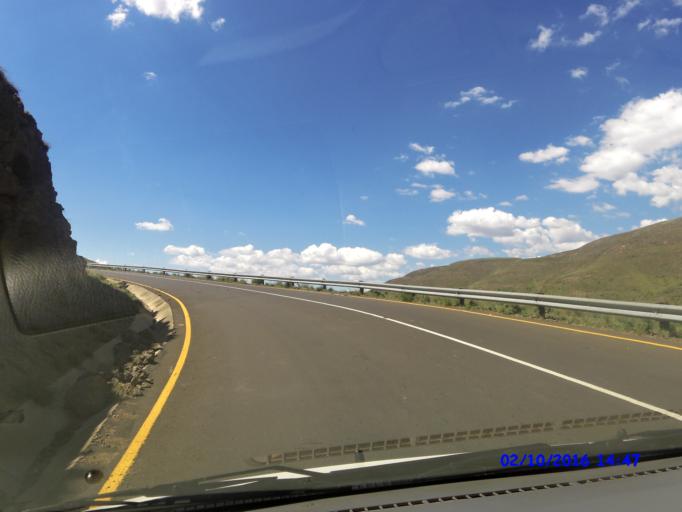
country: LS
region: Maseru
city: Nako
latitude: -29.5020
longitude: 28.0625
